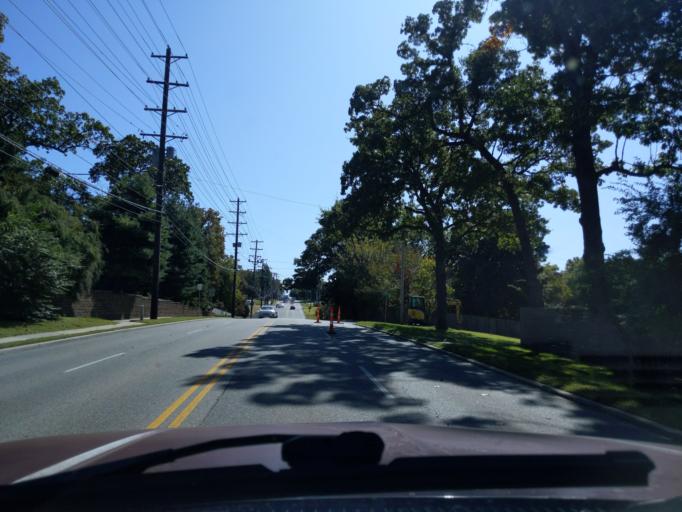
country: US
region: Oklahoma
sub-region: Tulsa County
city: Tulsa
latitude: 36.1136
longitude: -95.9581
